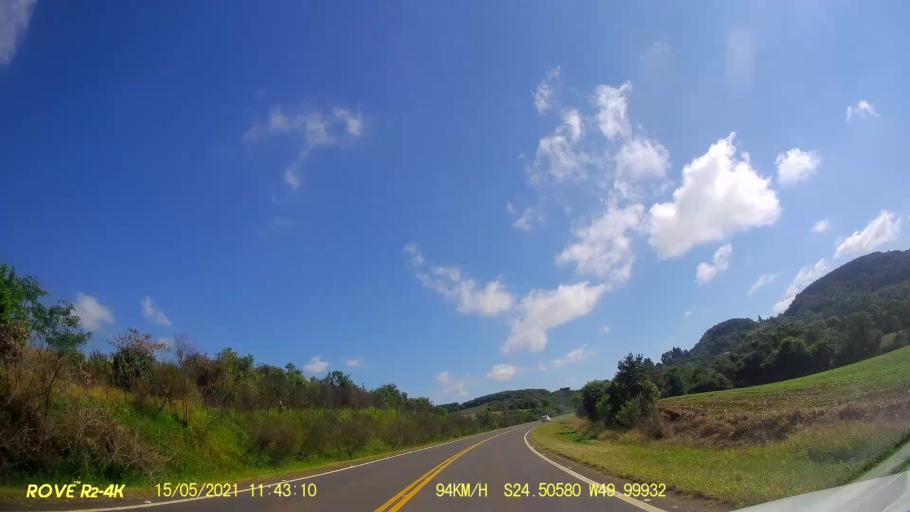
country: BR
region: Parana
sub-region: Pirai Do Sul
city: Pirai do Sul
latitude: -24.5042
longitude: -49.9974
